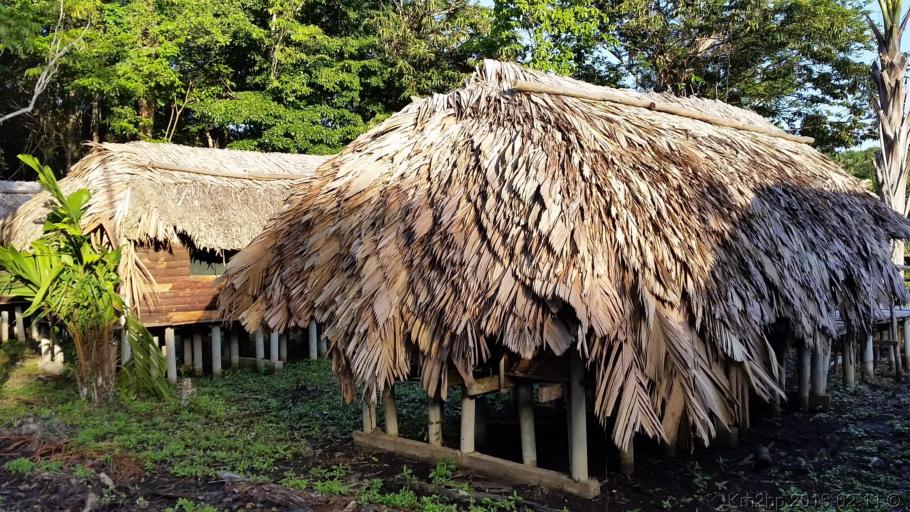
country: VE
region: Monagas
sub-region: Municipio Uracoa
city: Uracoa
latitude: 9.4147
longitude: -62.4644
